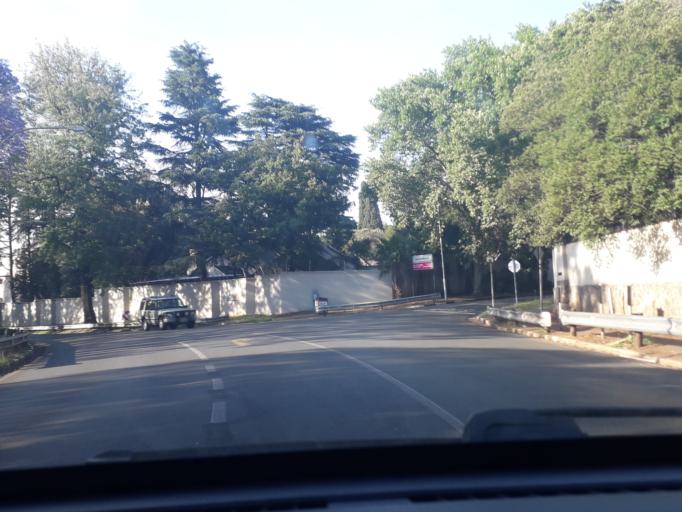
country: ZA
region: Gauteng
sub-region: City of Johannesburg Metropolitan Municipality
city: Johannesburg
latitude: -26.1601
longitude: 28.0353
